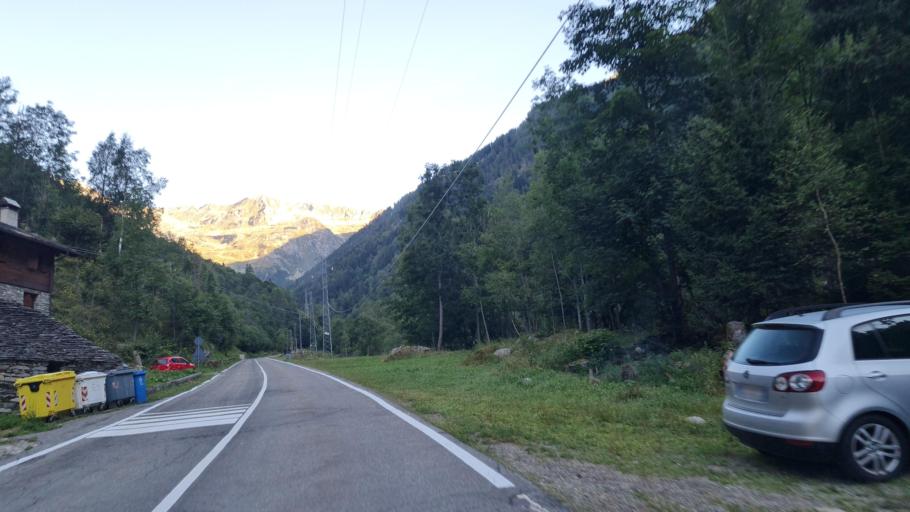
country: IT
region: Piedmont
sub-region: Provincia di Vercelli
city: Rima
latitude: 45.8727
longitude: 8.0193
